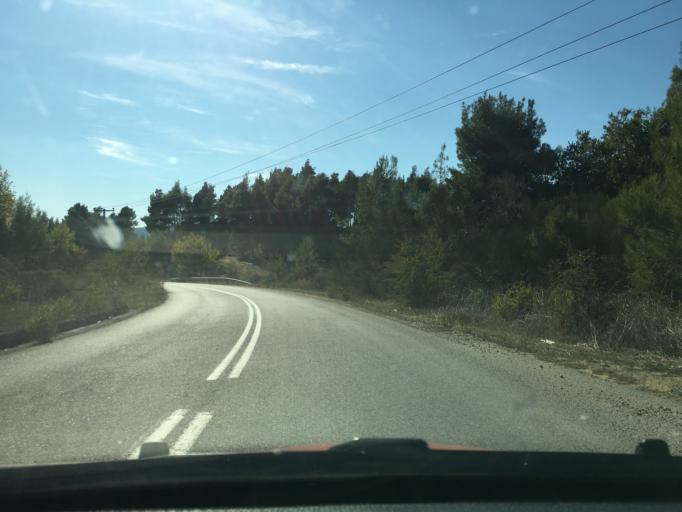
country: GR
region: Central Macedonia
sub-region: Nomos Chalkidikis
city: Ierissos
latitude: 40.3915
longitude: 23.8037
